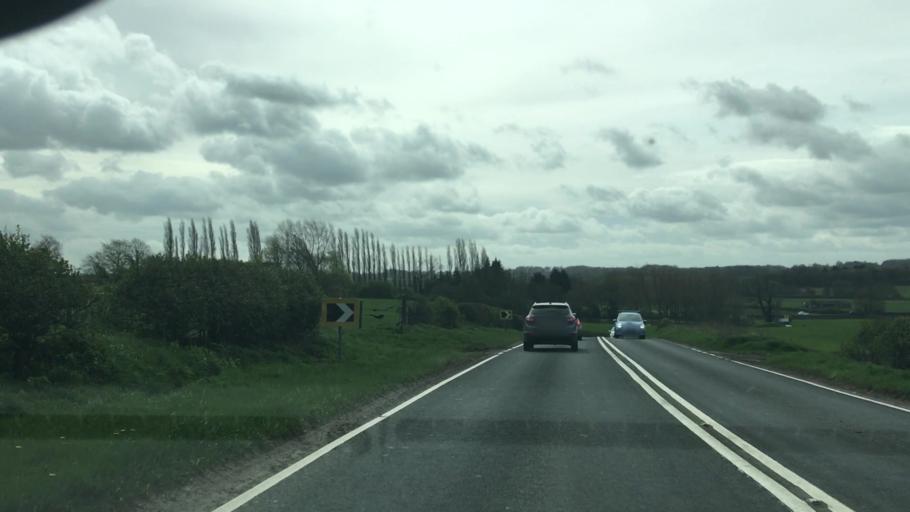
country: GB
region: England
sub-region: North Yorkshire
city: Knaresborough
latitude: 53.9595
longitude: -1.4425
